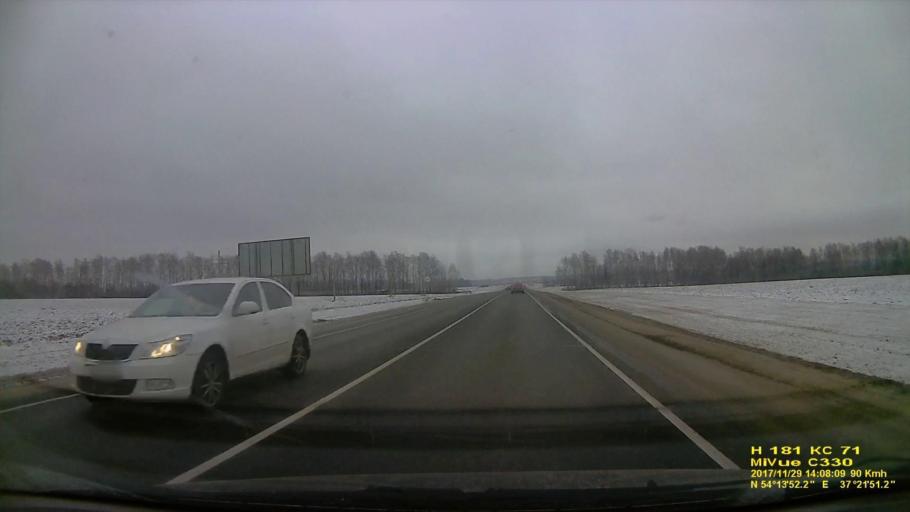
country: RU
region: Tula
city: Leninskiy
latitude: 54.2313
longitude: 37.3641
